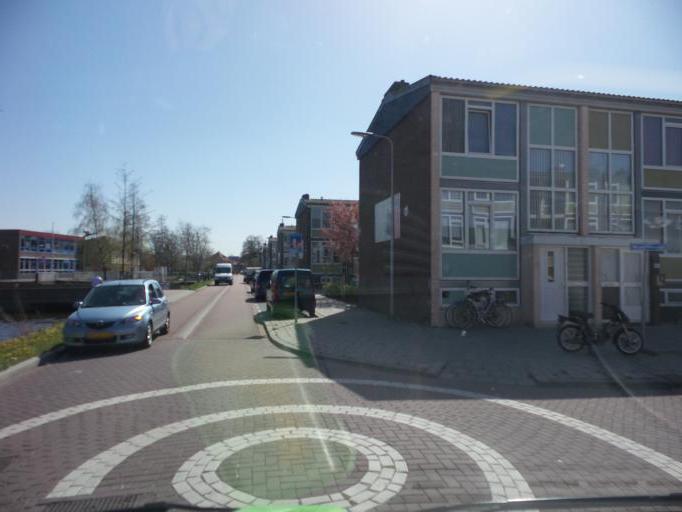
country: NL
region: South Holland
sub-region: Gemeente Gouda
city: Gouda
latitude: 52.0159
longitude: 4.6985
